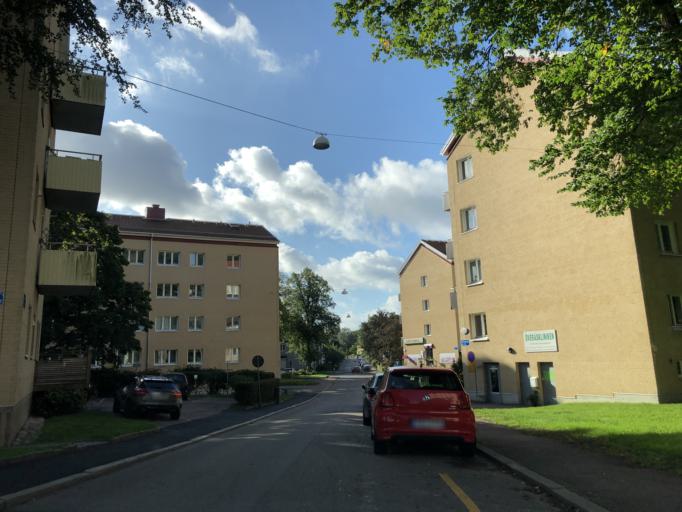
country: SE
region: Vaestra Goetaland
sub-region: Goteborg
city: Goeteborg
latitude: 57.7073
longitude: 11.9998
